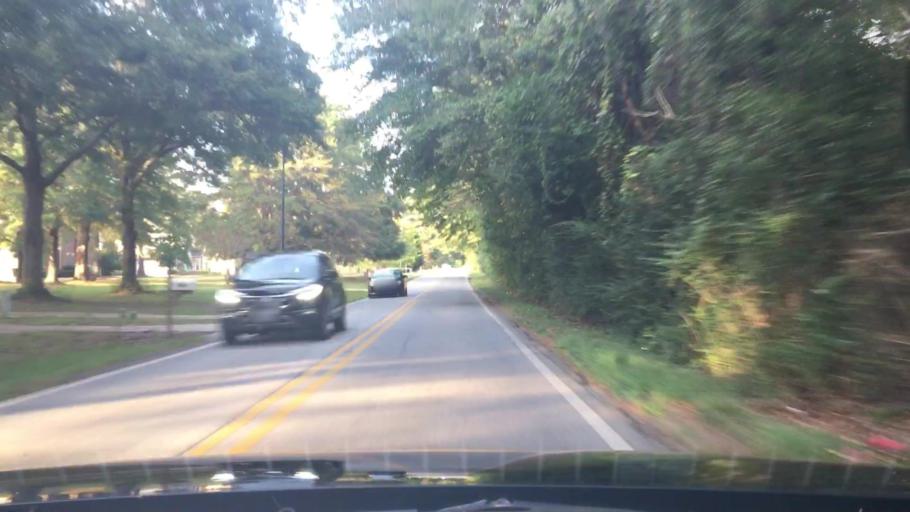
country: US
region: Georgia
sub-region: Coweta County
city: East Newnan
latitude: 33.3906
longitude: -84.7133
